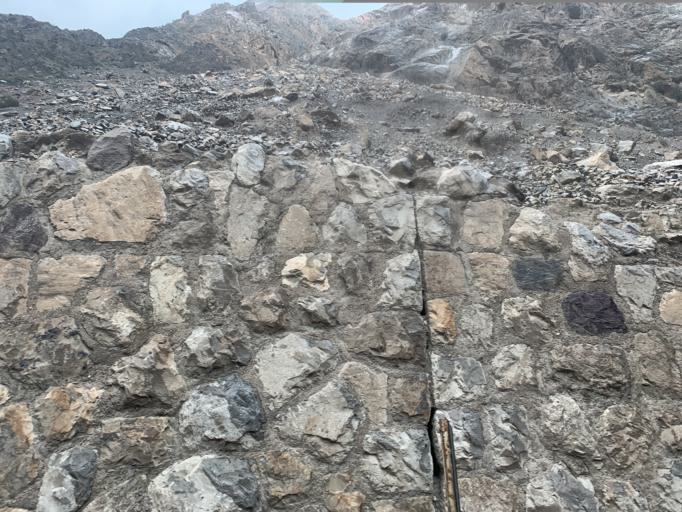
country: IR
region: Mazandaran
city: Amol
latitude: 36.1096
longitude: 52.2794
